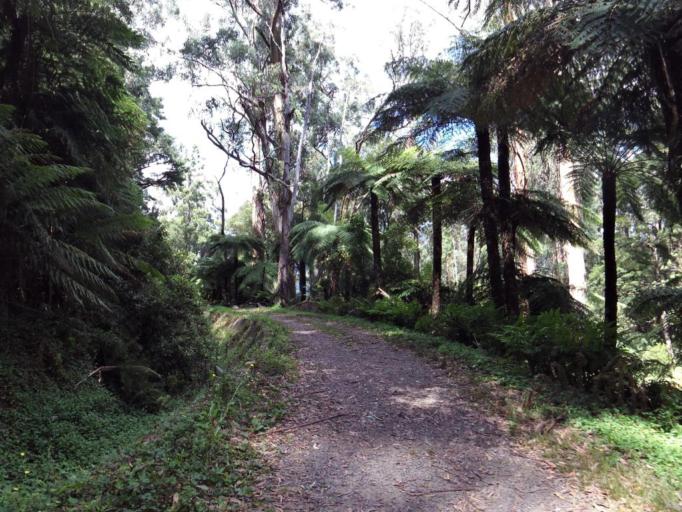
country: AU
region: Victoria
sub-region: Yarra Ranges
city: Millgrove
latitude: -37.7440
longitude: 145.7020
